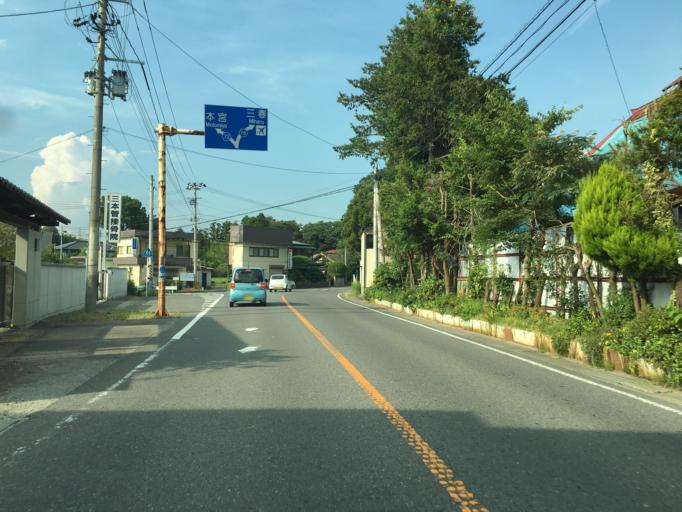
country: JP
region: Fukushima
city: Miharu
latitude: 37.4517
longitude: 140.4292
